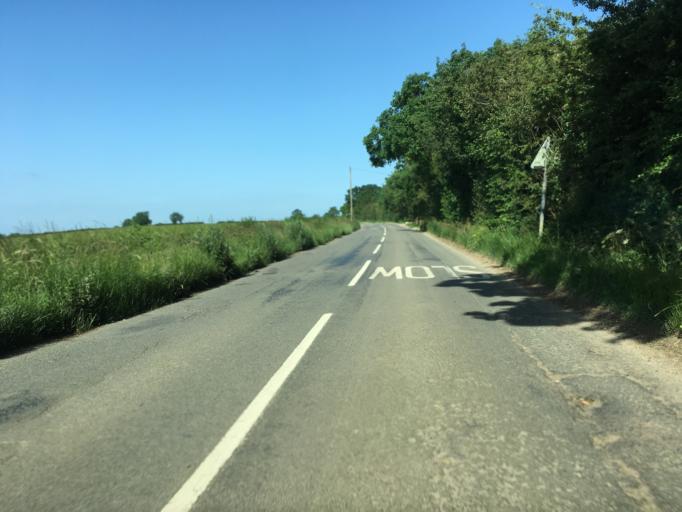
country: GB
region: England
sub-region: Buckinghamshire
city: Newton Longville
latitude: 51.9623
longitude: -0.7504
